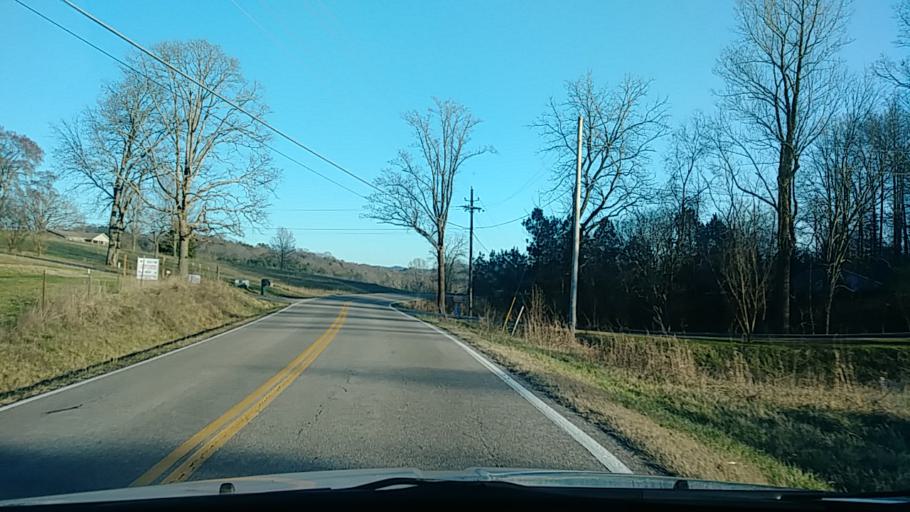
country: US
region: Tennessee
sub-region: Hamblen County
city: Morristown
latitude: 36.1990
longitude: -83.4003
